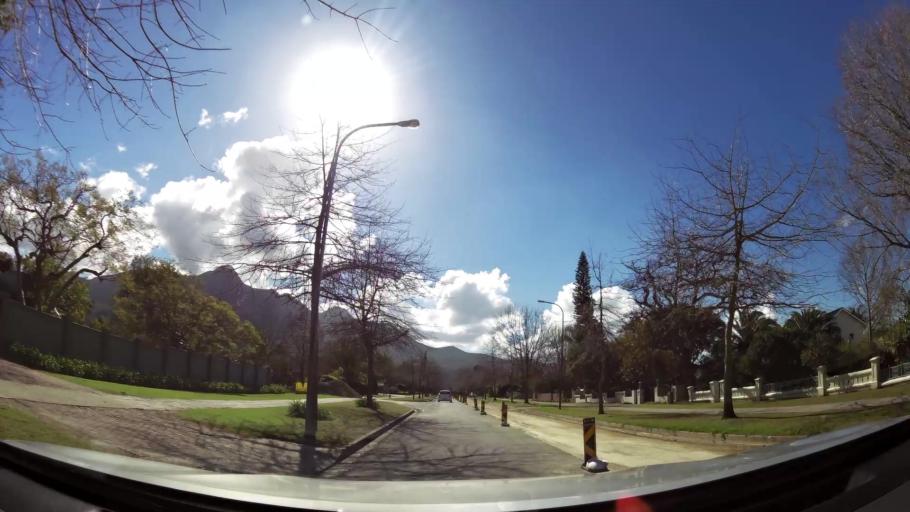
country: ZA
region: Western Cape
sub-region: Eden District Municipality
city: George
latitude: -33.9512
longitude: 22.4614
